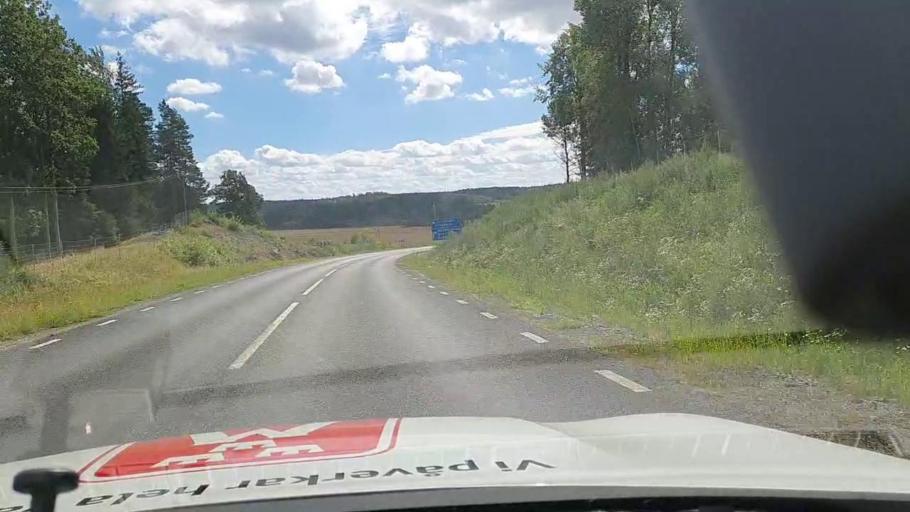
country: SE
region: Soedermanland
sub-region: Nykopings Kommun
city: Olstorp
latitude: 58.7512
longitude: 16.6162
